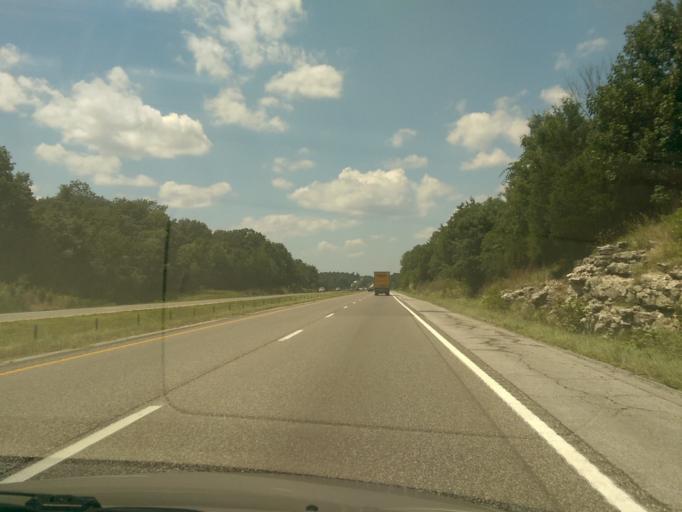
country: US
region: Missouri
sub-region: Boone County
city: Columbia
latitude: 38.9728
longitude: -92.4639
